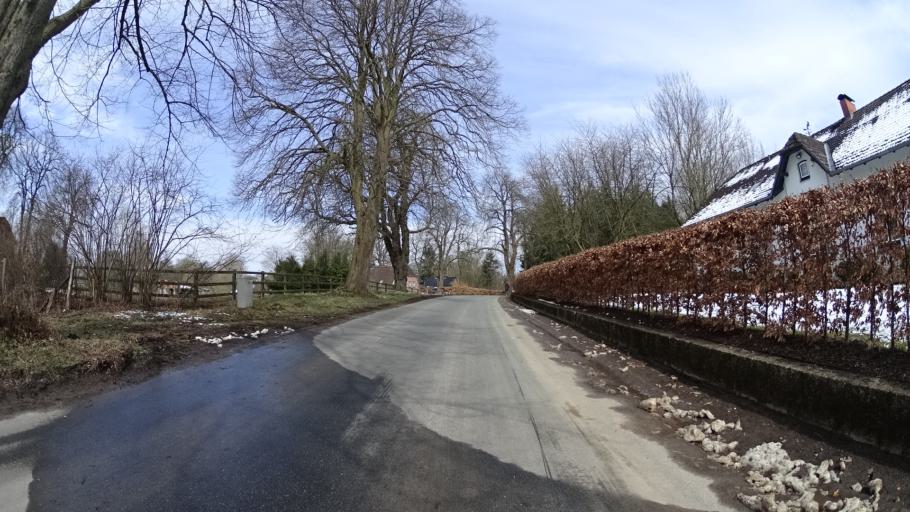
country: DE
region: Schleswig-Holstein
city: Stolpe
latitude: 54.1555
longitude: 10.2348
